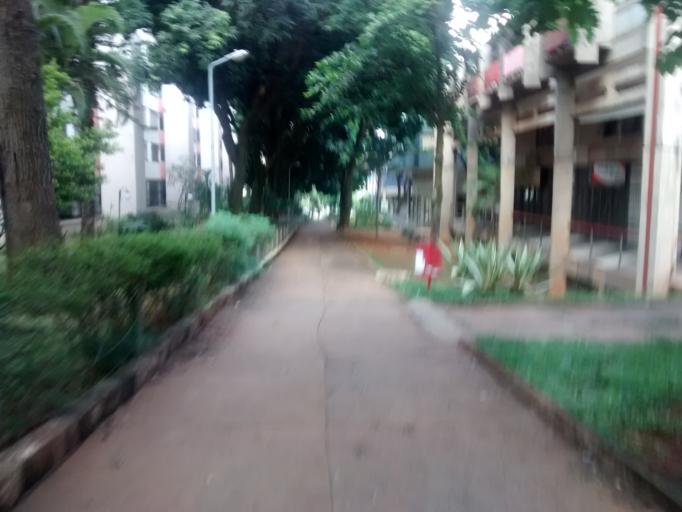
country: BR
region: Federal District
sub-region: Brasilia
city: Brasilia
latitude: -15.7499
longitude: -47.8934
